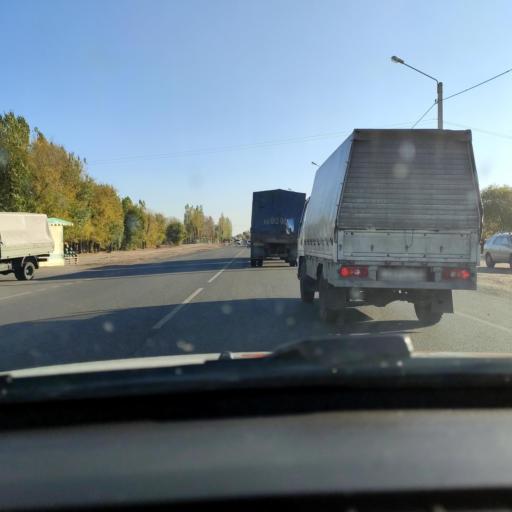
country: RU
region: Voronezj
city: Pridonskoy
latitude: 51.7072
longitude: 39.0744
